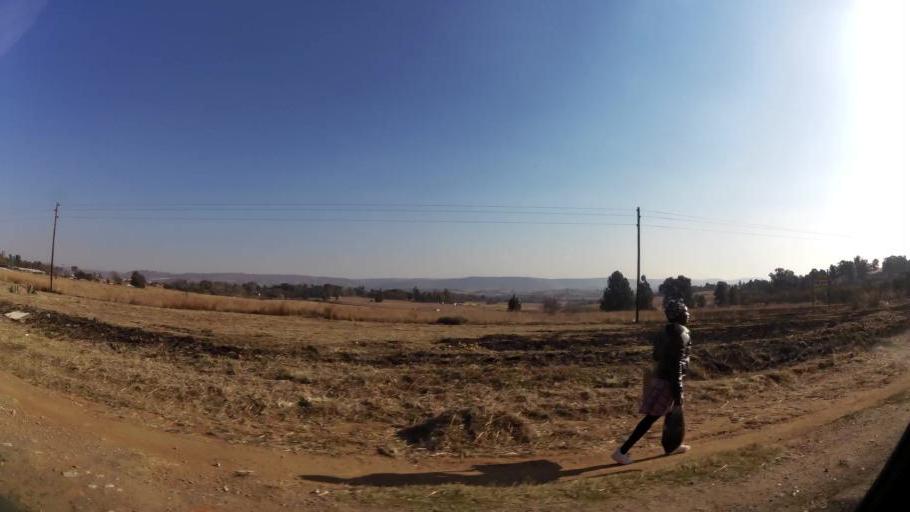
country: ZA
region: Gauteng
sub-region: West Rand District Municipality
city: Muldersdriseloop
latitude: -26.0467
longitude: 27.8888
